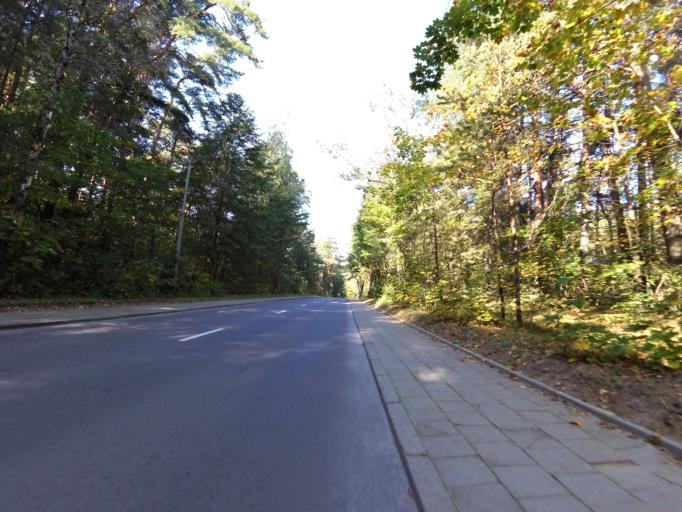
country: LT
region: Vilnius County
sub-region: Vilnius
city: Vilnius
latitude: 54.7301
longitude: 25.3104
